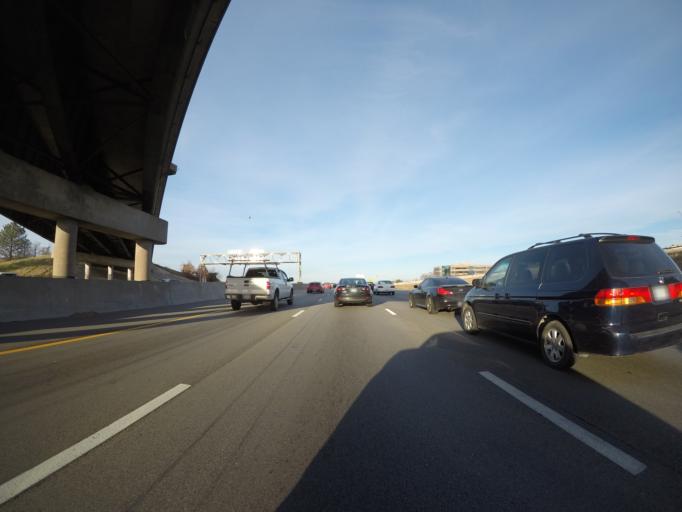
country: US
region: Kansas
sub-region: Johnson County
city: Lenexa
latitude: 38.9763
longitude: -94.7138
